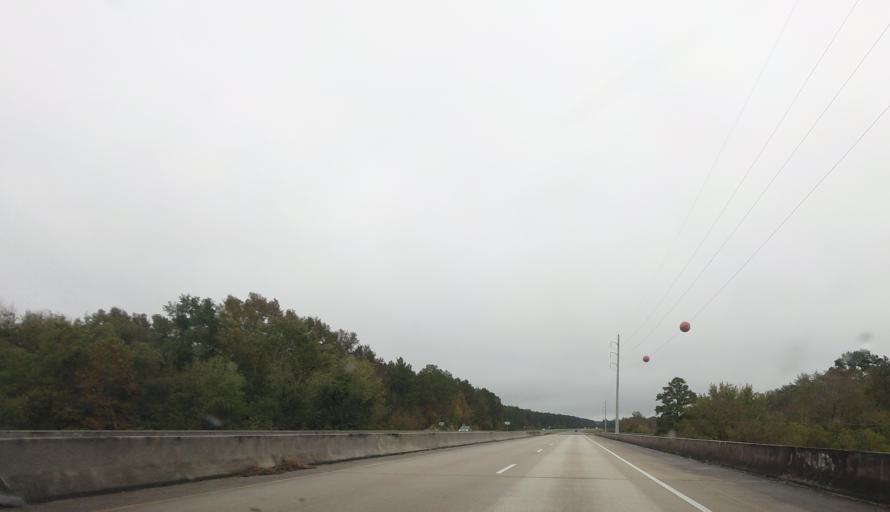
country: US
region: Georgia
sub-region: Taylor County
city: Reynolds
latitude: 32.5432
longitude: -84.0147
